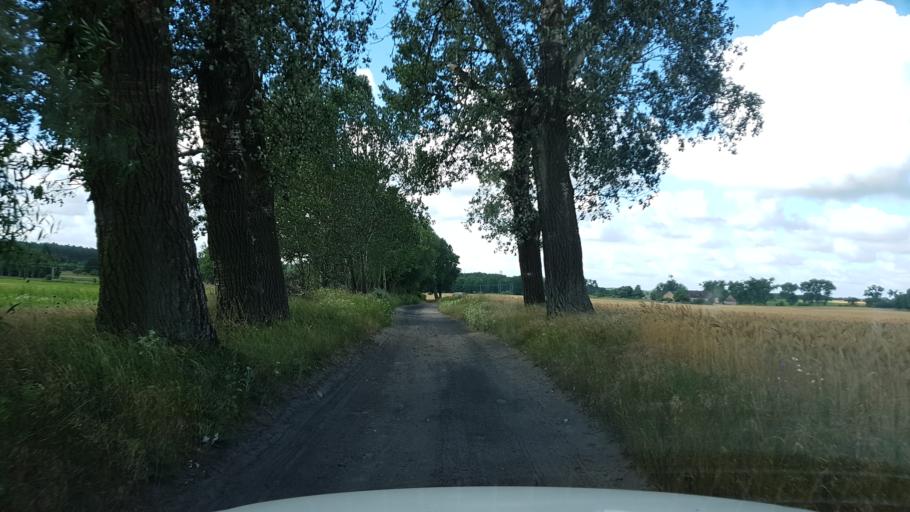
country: PL
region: West Pomeranian Voivodeship
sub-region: Powiat mysliborski
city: Debno
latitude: 52.7188
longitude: 14.6555
